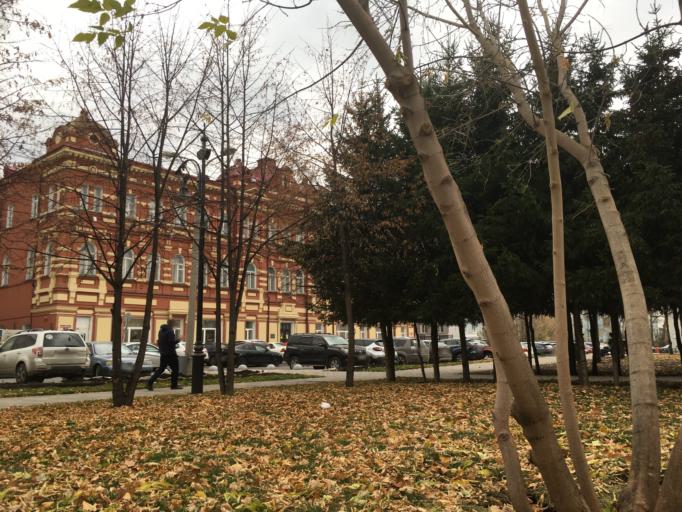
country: RU
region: Tomsk
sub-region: Tomskiy Rayon
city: Tomsk
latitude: 56.4831
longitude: 84.9473
